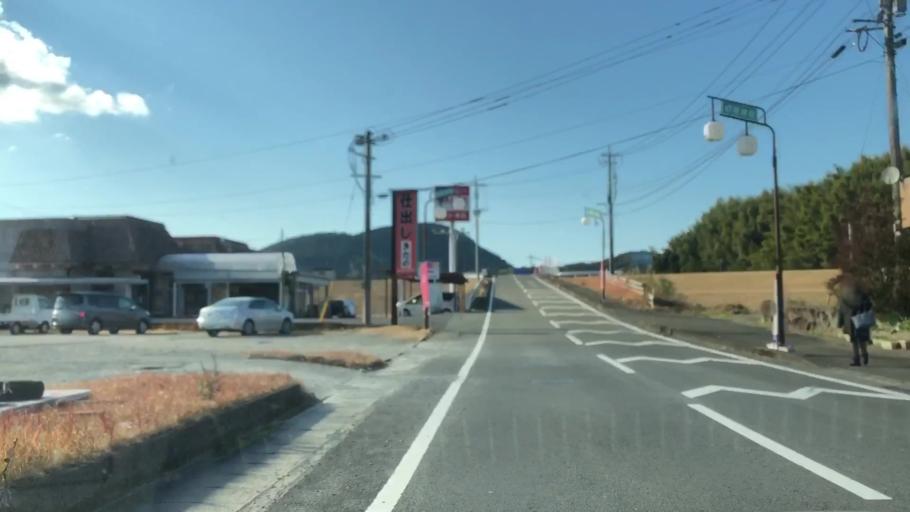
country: JP
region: Kagoshima
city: Satsumasendai
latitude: 31.8644
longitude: 130.3320
